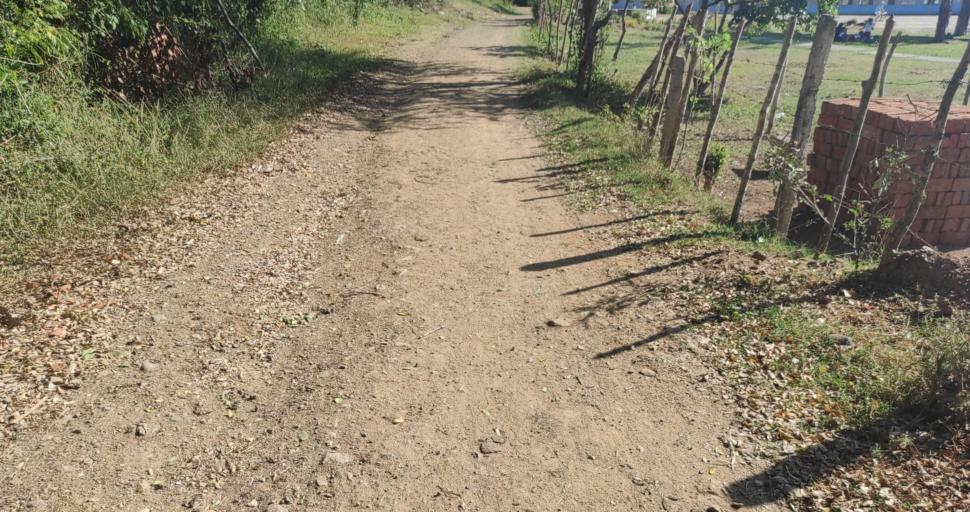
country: CU
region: Santiago de Cuba
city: Segundo Frente
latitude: 20.4382
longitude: -75.5042
